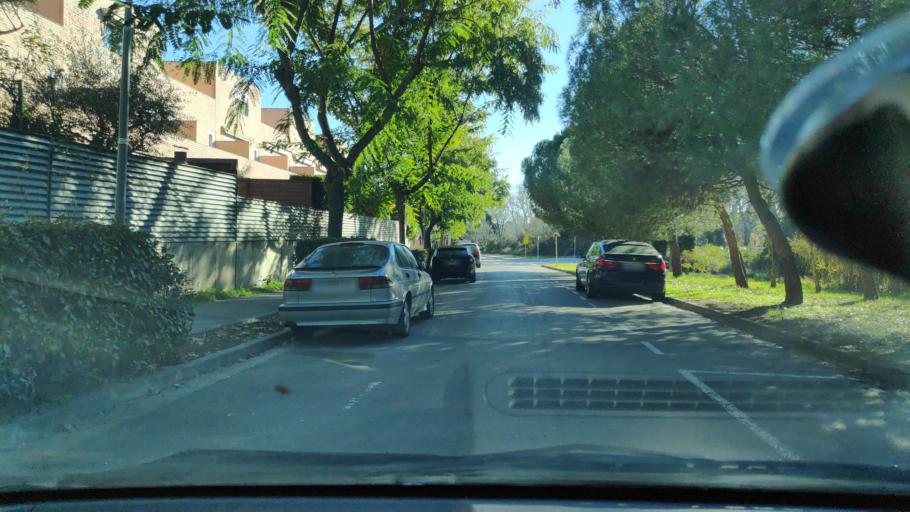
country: ES
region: Catalonia
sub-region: Provincia de Barcelona
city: Sant Quirze del Valles
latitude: 41.5420
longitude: 2.0681
